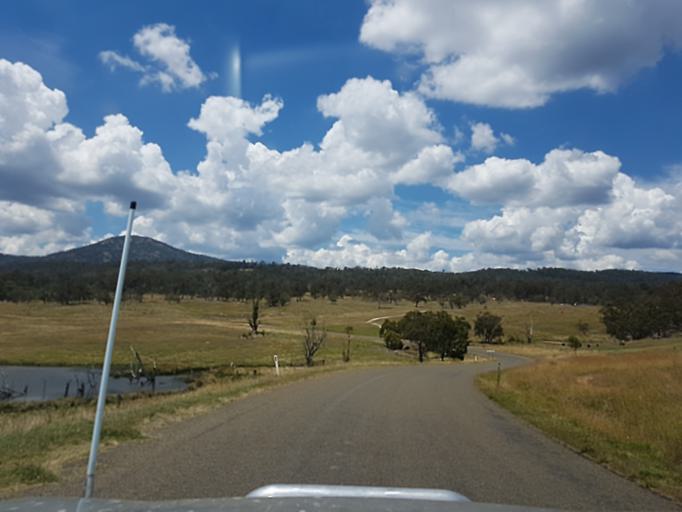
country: AU
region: Victoria
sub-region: Alpine
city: Mount Beauty
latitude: -36.9000
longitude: 147.8618
